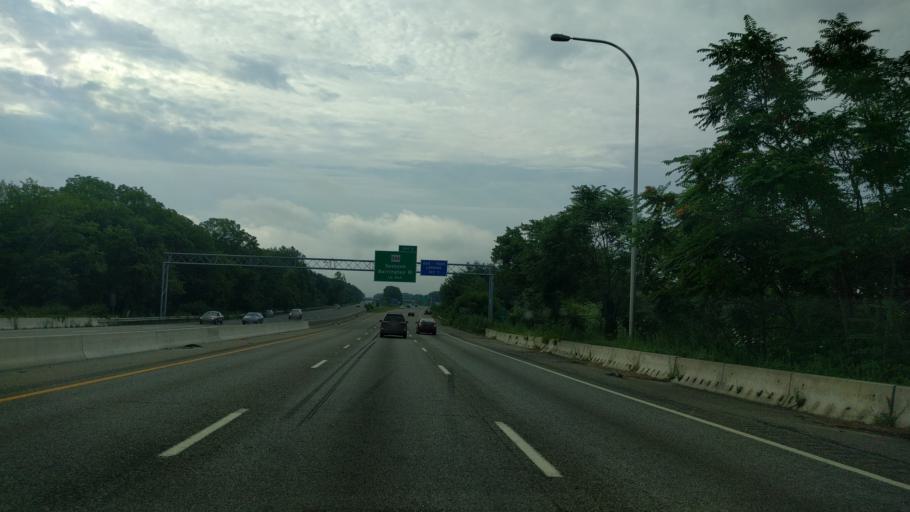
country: US
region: Massachusetts
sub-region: Bristol County
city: Seekonk
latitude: 41.8069
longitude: -71.3400
